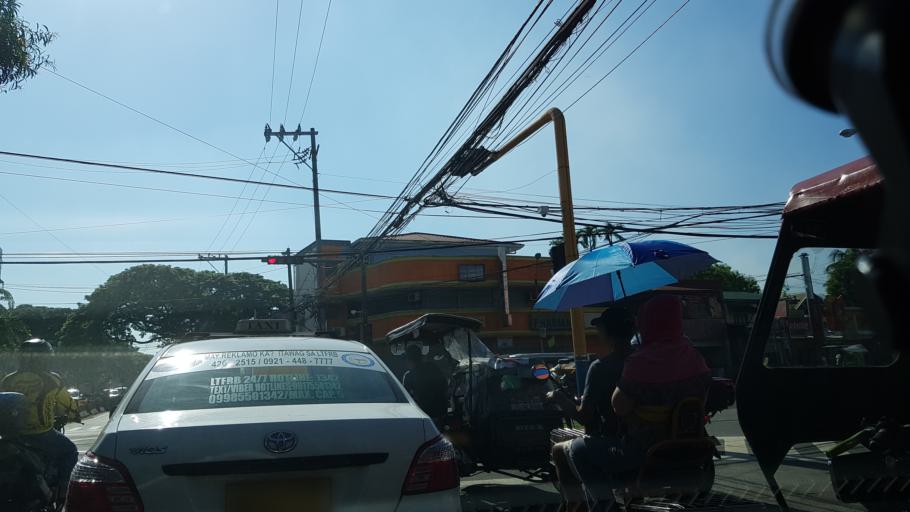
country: PH
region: Metro Manila
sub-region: Pasig
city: Pasig City
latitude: 14.5685
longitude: 121.0858
